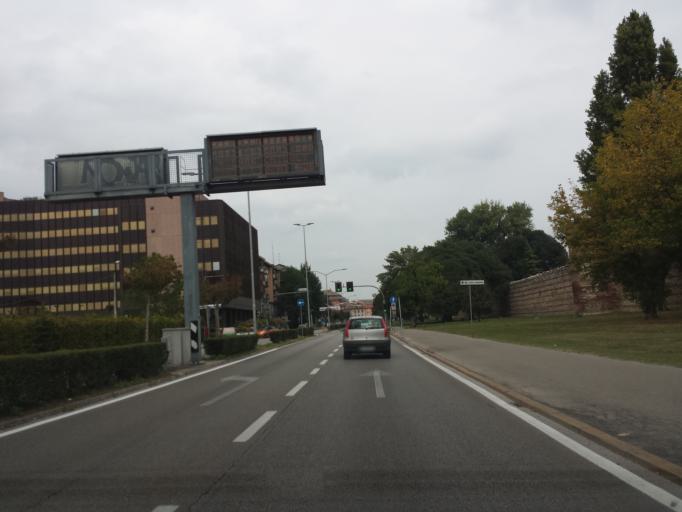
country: IT
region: Veneto
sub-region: Provincia di Vicenza
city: Vicenza
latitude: 45.5486
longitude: 11.5349
